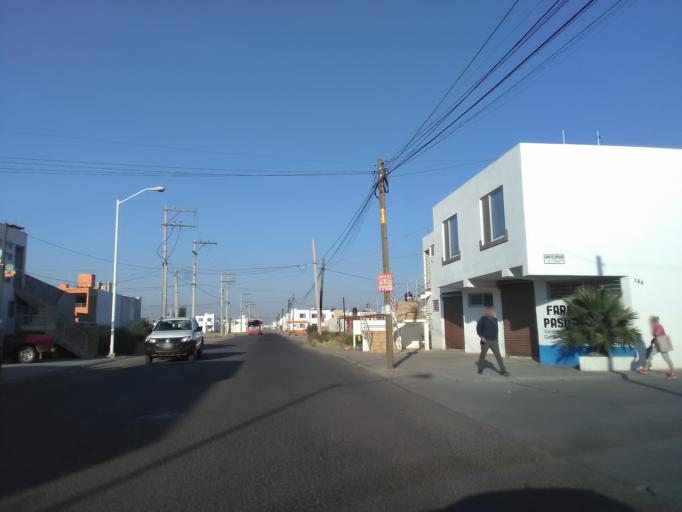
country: MX
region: Durango
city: Victoria de Durango
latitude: 24.0622
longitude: -104.6170
